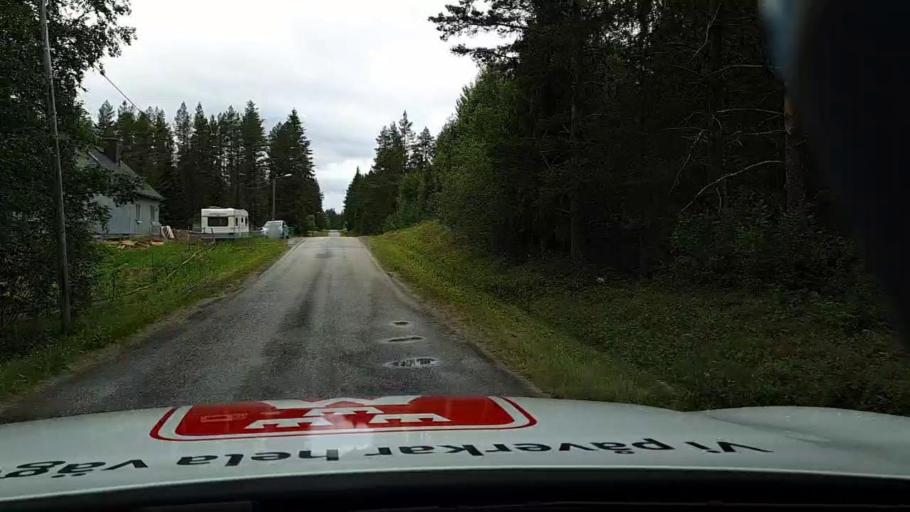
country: SE
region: Vaesterbotten
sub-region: Dorotea Kommun
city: Dorotea
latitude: 64.0996
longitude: 16.4073
